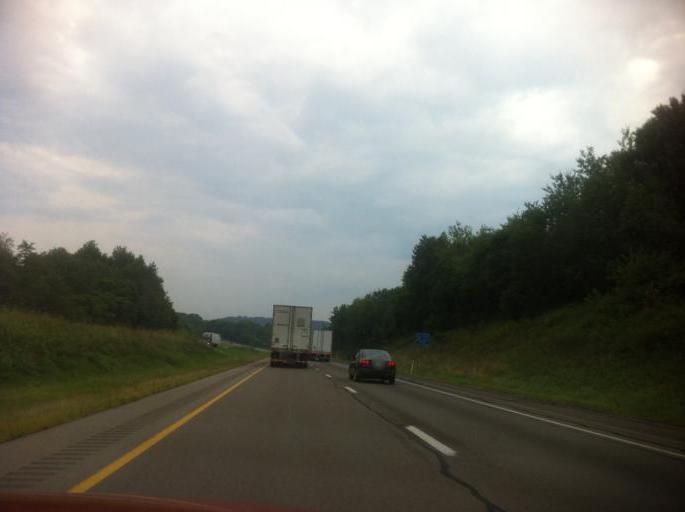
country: US
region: Pennsylvania
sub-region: Jefferson County
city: Brookville
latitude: 41.1861
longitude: -79.1675
